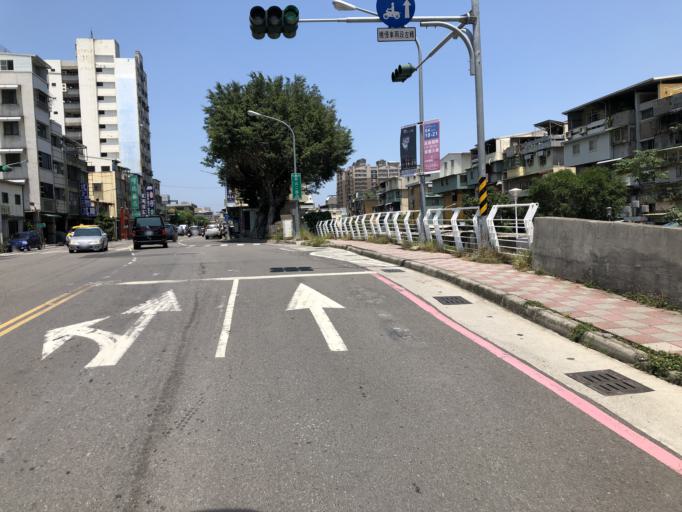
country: TW
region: Kaohsiung
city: Kaohsiung
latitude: 22.6297
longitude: 120.2806
